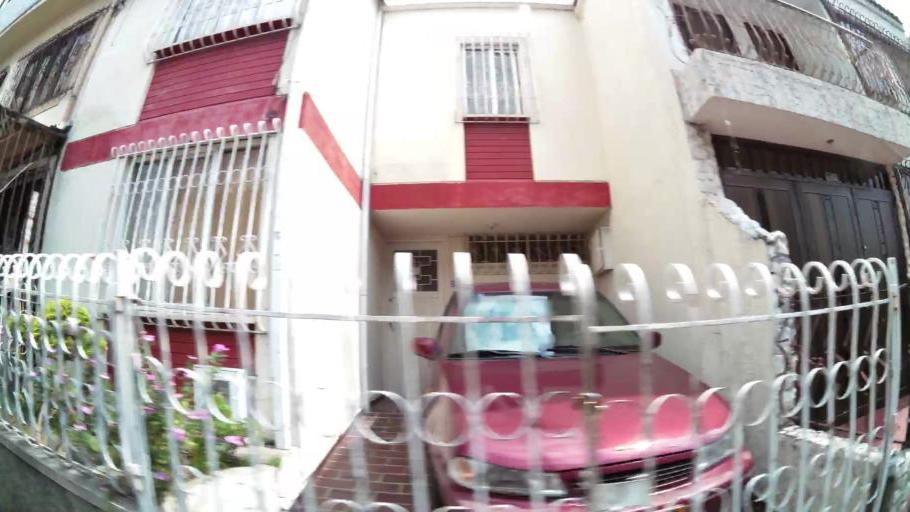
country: CO
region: Valle del Cauca
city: Cali
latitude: 3.4854
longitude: -76.5080
